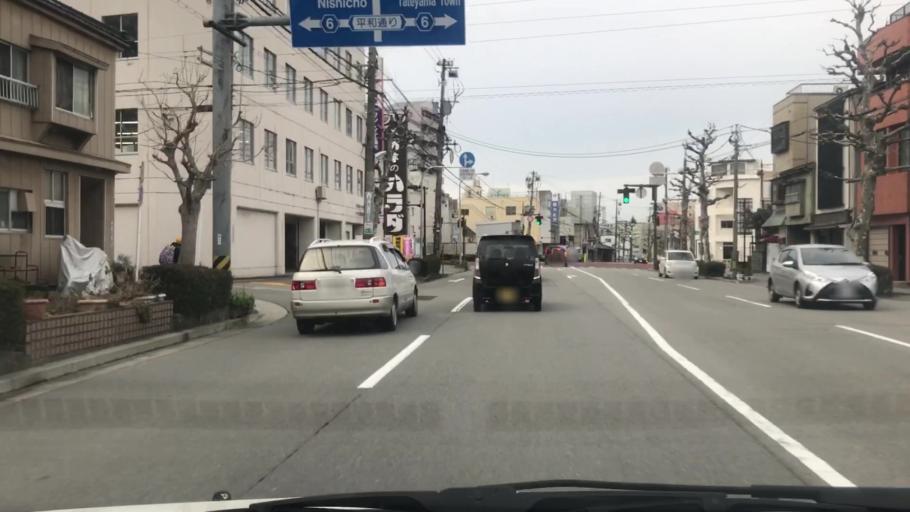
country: JP
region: Toyama
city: Toyama-shi
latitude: 36.6881
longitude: 137.2214
